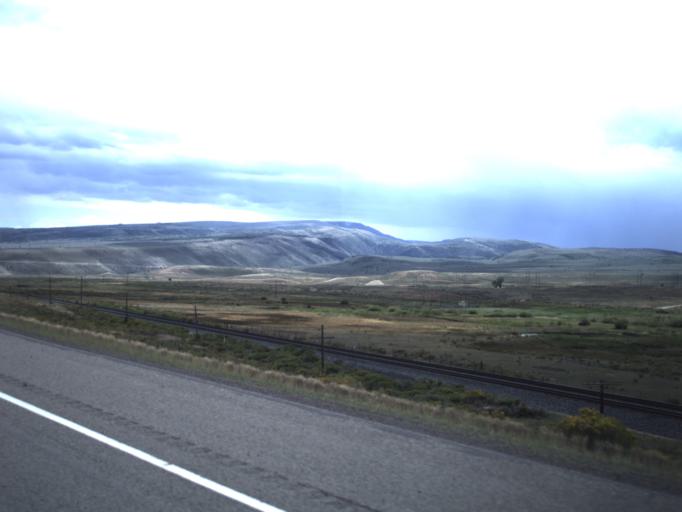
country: US
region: Utah
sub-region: Carbon County
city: Helper
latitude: 39.8585
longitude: -111.0232
